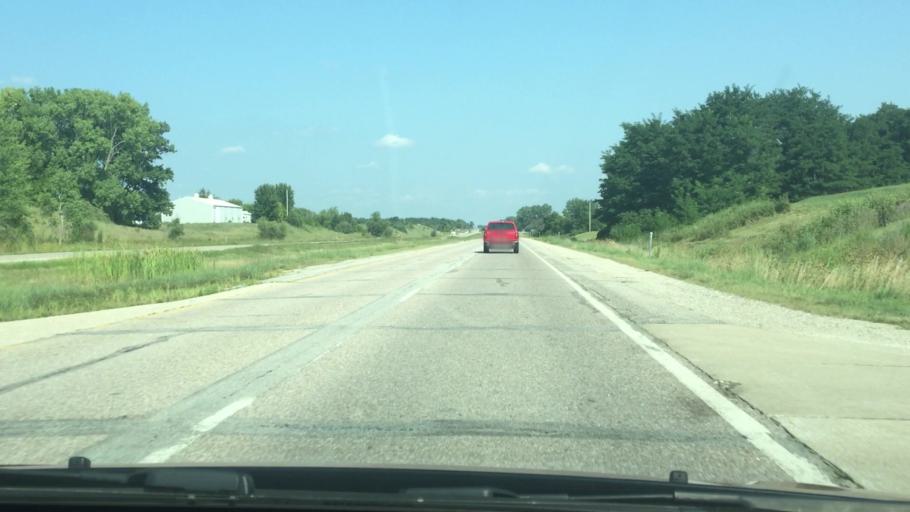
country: US
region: Iowa
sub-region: Scott County
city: Blue Grass
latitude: 41.5185
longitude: -90.8516
